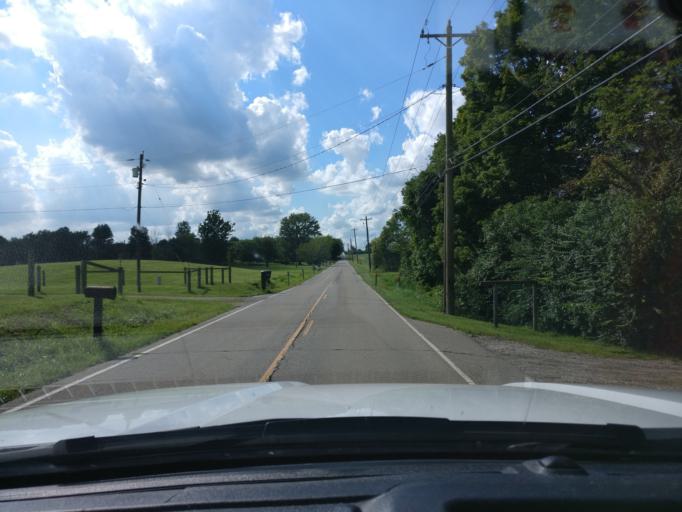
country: US
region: Ohio
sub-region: Warren County
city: Springboro
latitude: 39.5065
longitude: -84.2309
